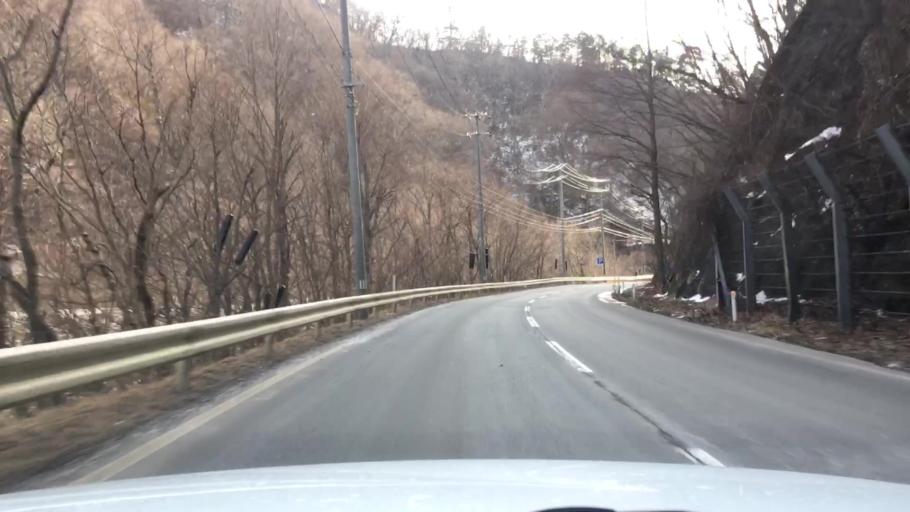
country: JP
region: Iwate
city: Tono
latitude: 39.6363
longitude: 141.5369
